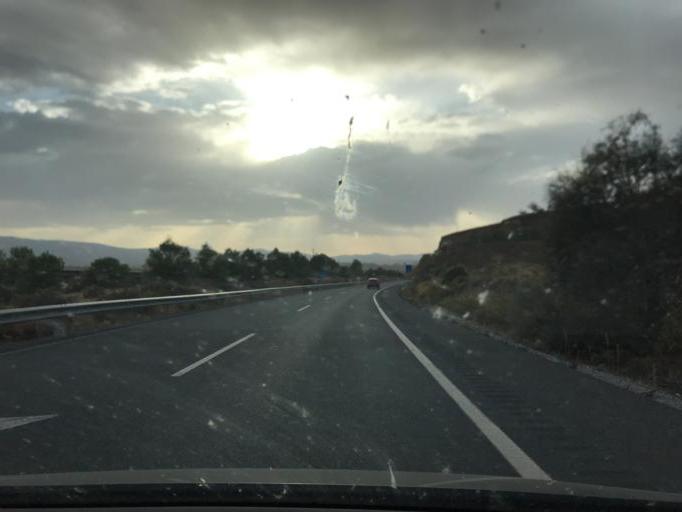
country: ES
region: Andalusia
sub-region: Provincia de Granada
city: Guadix
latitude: 37.3220
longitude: -3.1144
